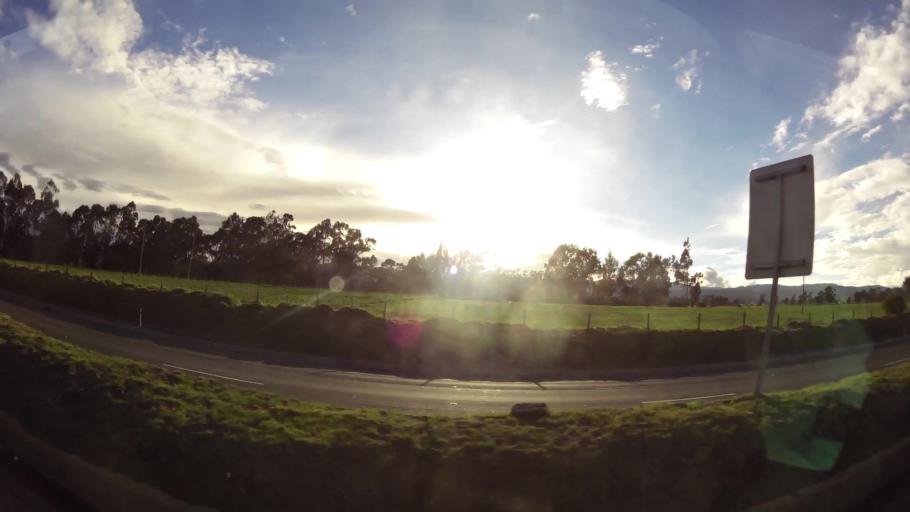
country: EC
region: Cotopaxi
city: Saquisili
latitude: -0.8297
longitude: -78.6192
